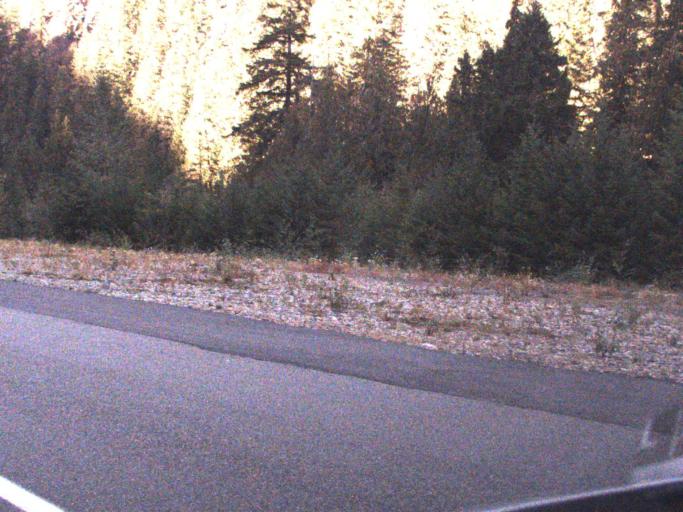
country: US
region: Washington
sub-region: Snohomish County
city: Darrington
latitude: 48.6855
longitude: -120.8856
